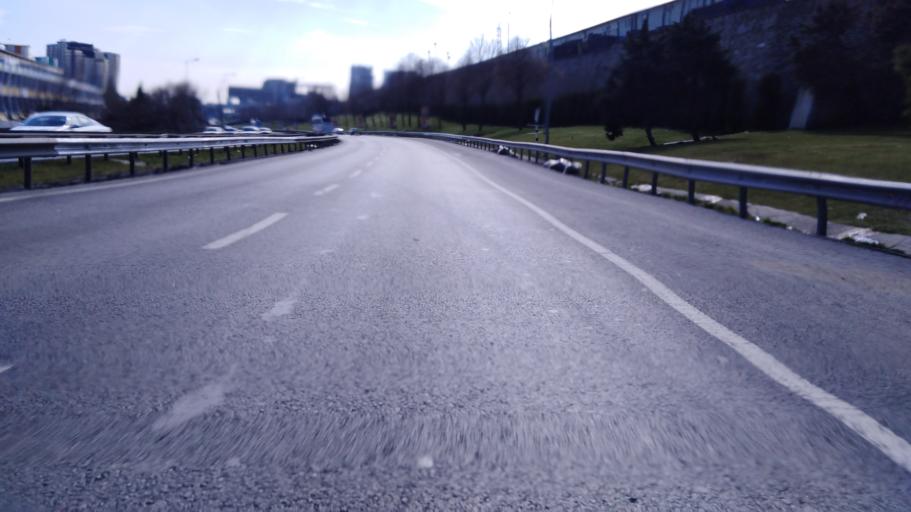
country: TR
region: Istanbul
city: Esenler
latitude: 41.0540
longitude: 28.8892
